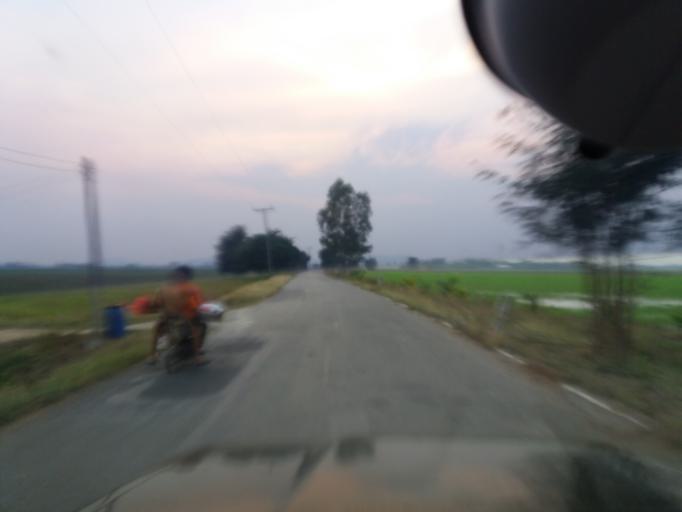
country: TH
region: Suphan Buri
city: Doem Bang Nang Buat
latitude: 14.8889
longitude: 100.1515
